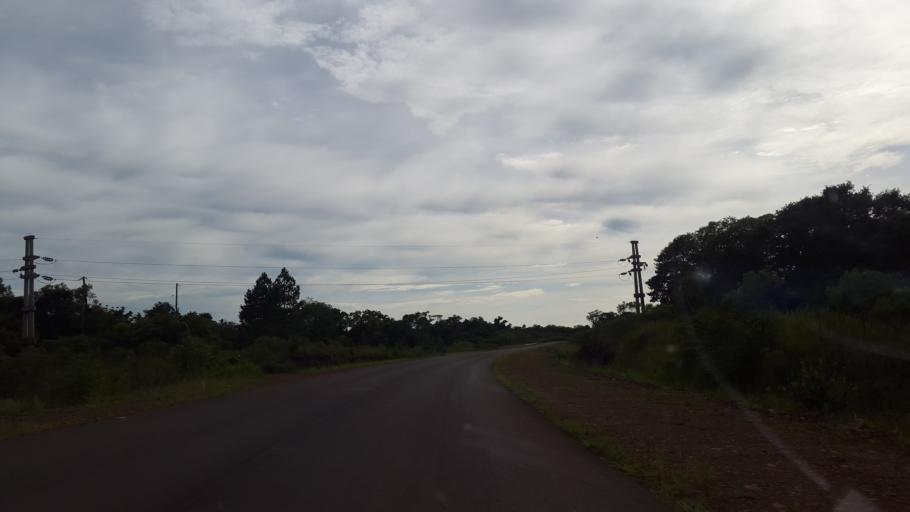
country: AR
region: Misiones
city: Bernardo de Irigoyen
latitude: -26.4213
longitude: -53.8369
